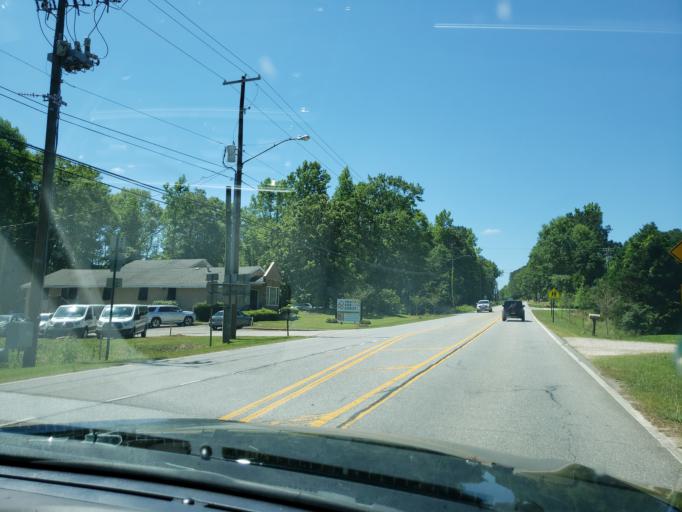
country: US
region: Alabama
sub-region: Lee County
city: Auburn
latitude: 32.6360
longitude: -85.4818
